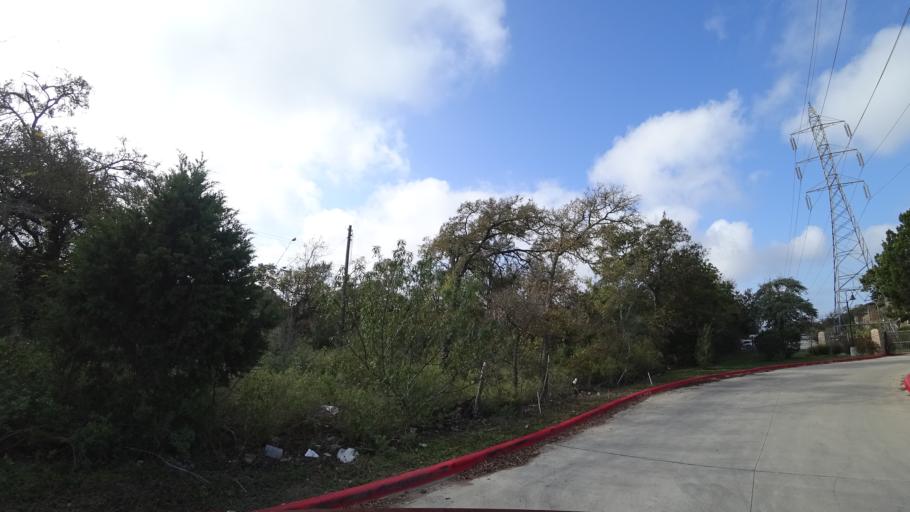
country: US
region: Texas
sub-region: Williamson County
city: Anderson Mill
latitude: 30.3987
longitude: -97.8468
